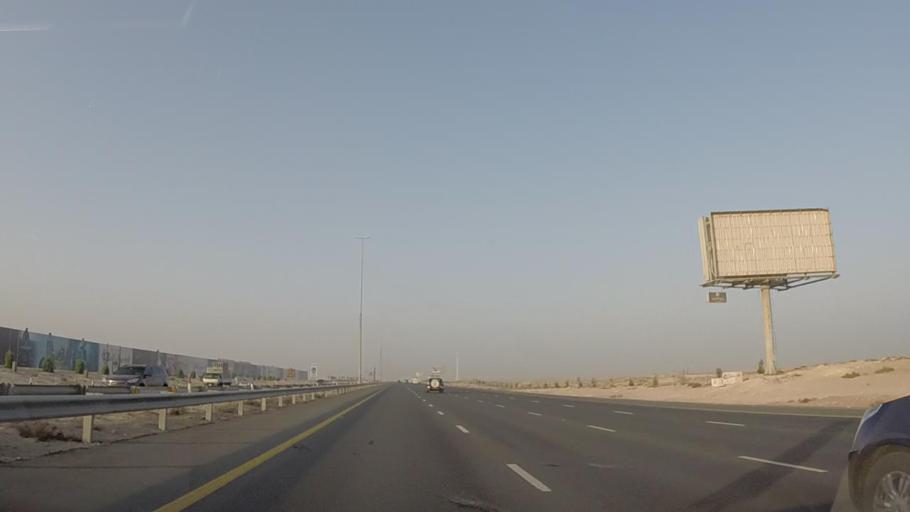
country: AE
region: Dubai
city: Dubai
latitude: 24.9192
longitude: 54.9817
